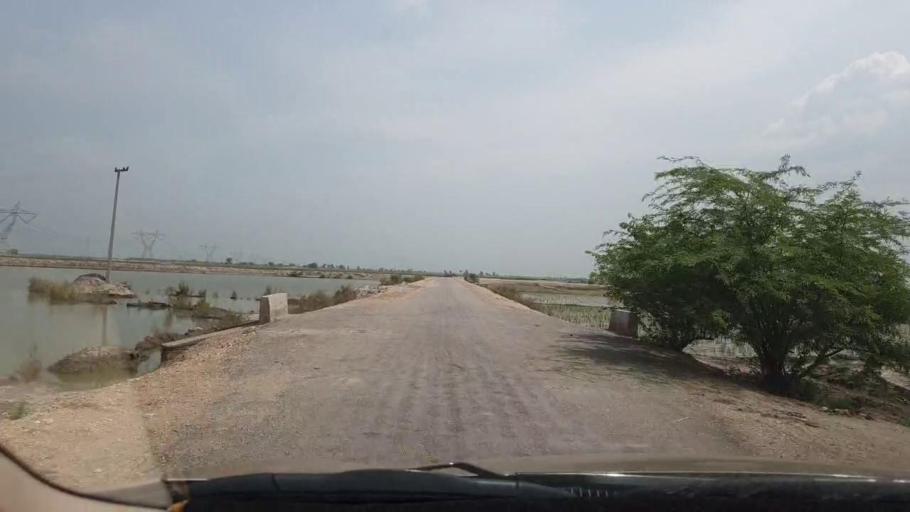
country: PK
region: Sindh
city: Goth Garelo
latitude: 27.5155
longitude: 68.1019
